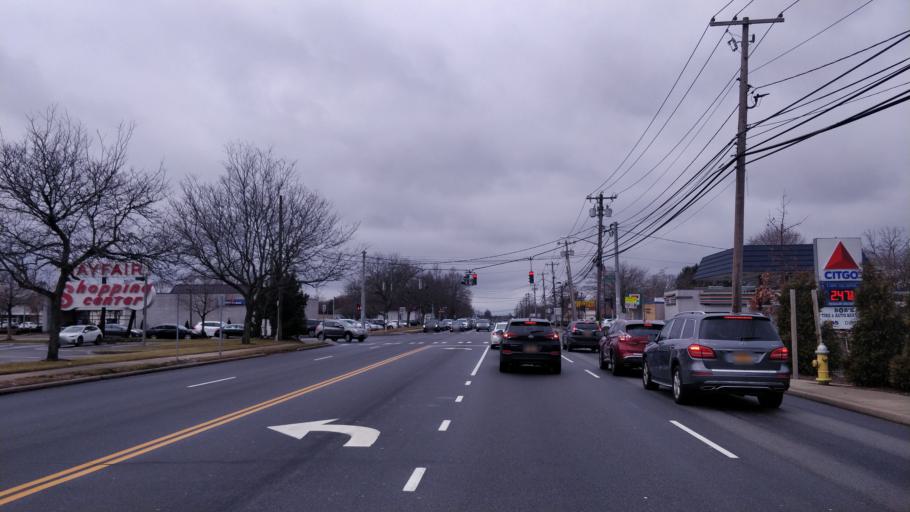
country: US
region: New York
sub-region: Suffolk County
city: Commack
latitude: 40.8452
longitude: -73.2725
